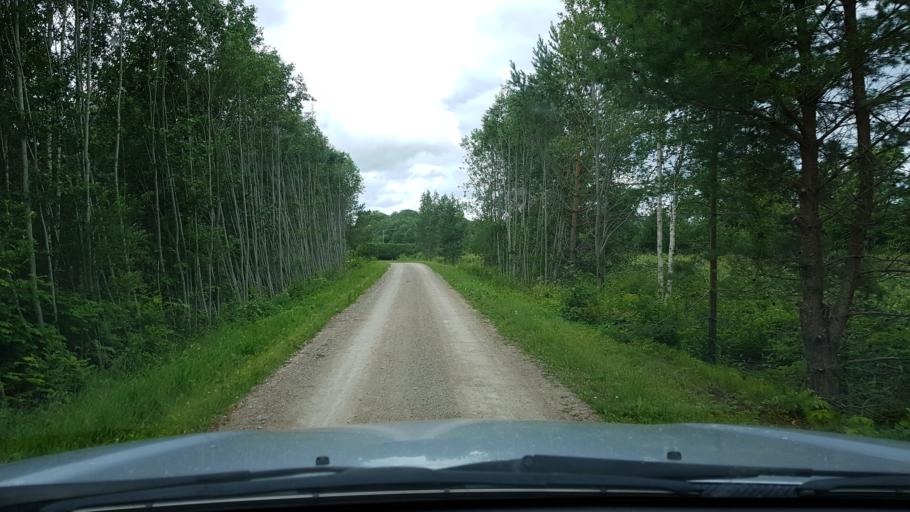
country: EE
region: Ida-Virumaa
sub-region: Narva-Joesuu linn
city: Narva-Joesuu
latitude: 59.4069
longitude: 27.9779
